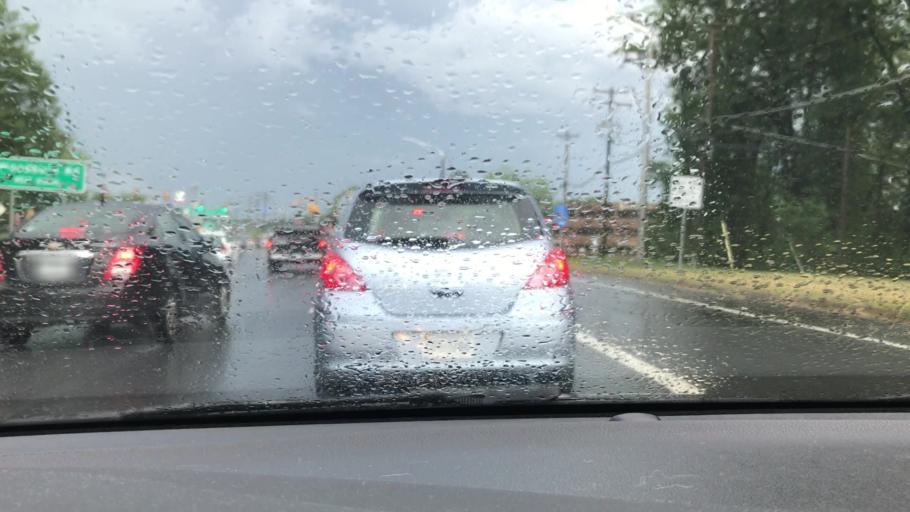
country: US
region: Virginia
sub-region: Fairfax County
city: Merrifield
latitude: 38.8557
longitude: -77.2246
